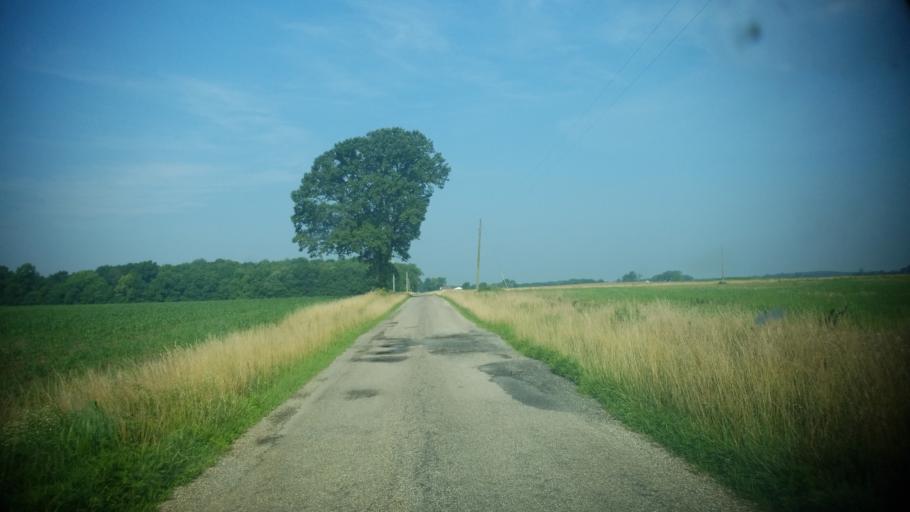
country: US
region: Illinois
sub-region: Clay County
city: Flora
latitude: 38.6030
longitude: -88.4272
